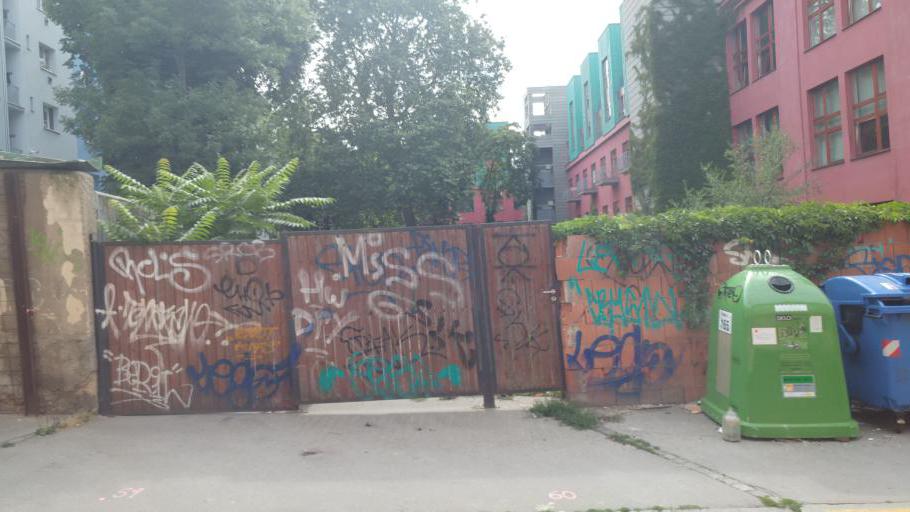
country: CZ
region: Praha
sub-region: Praha 8
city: Liben
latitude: 50.1041
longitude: 14.4793
